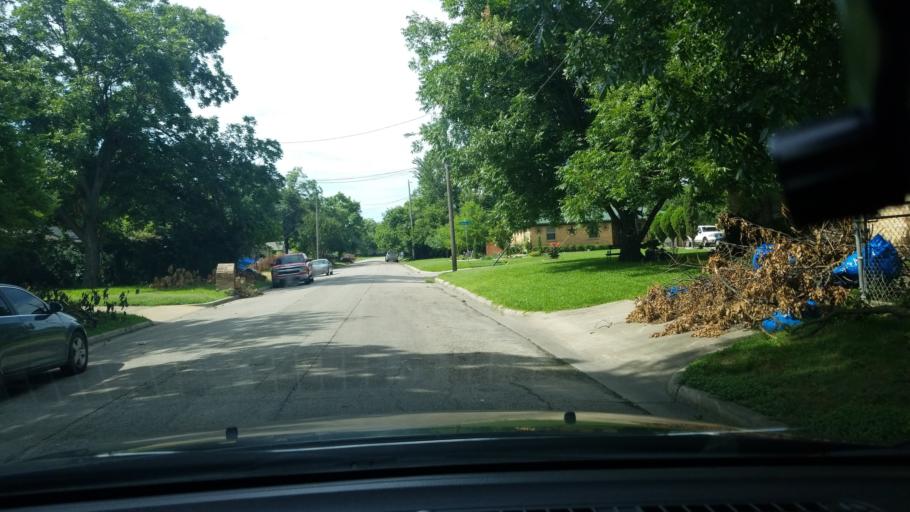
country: US
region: Texas
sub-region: Dallas County
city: Balch Springs
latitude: 32.7733
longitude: -96.6793
